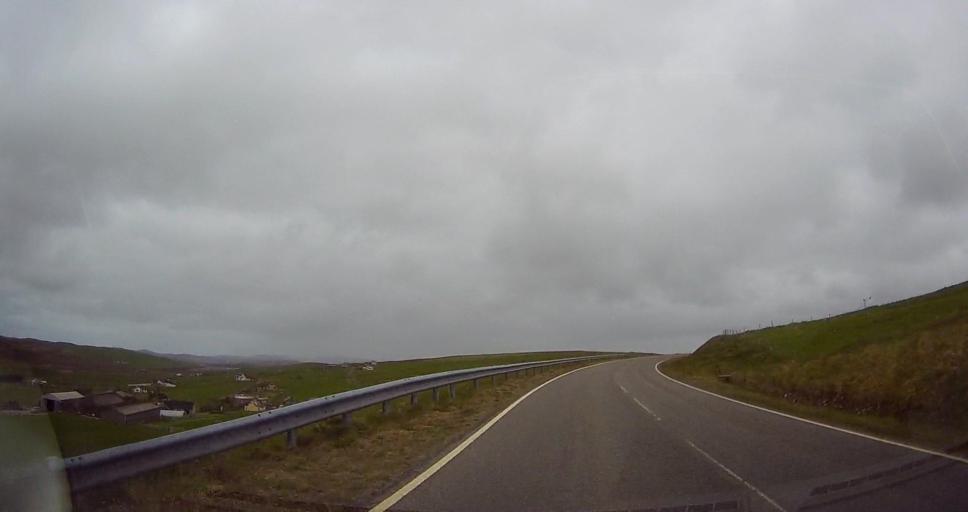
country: GB
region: Scotland
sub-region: Shetland Islands
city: Lerwick
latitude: 60.2604
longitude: -1.4055
